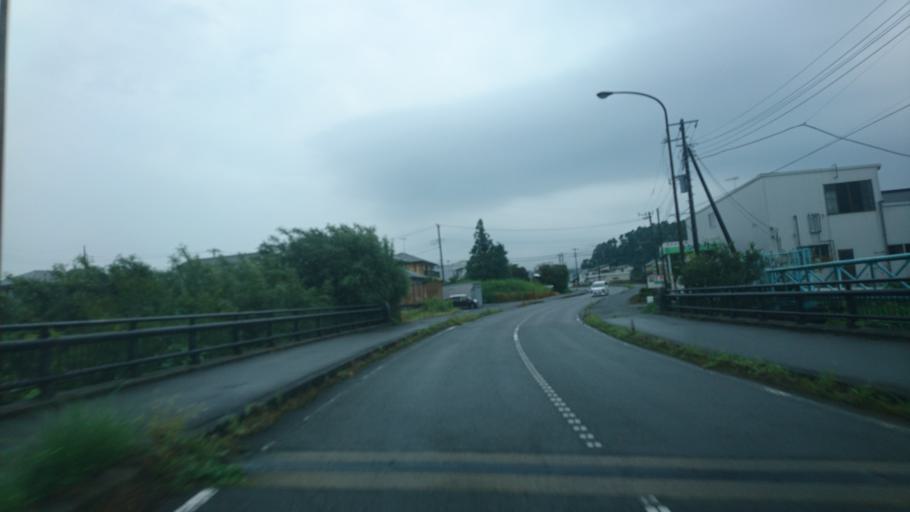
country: JP
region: Chiba
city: Kimitsu
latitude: 35.3048
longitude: 139.9450
